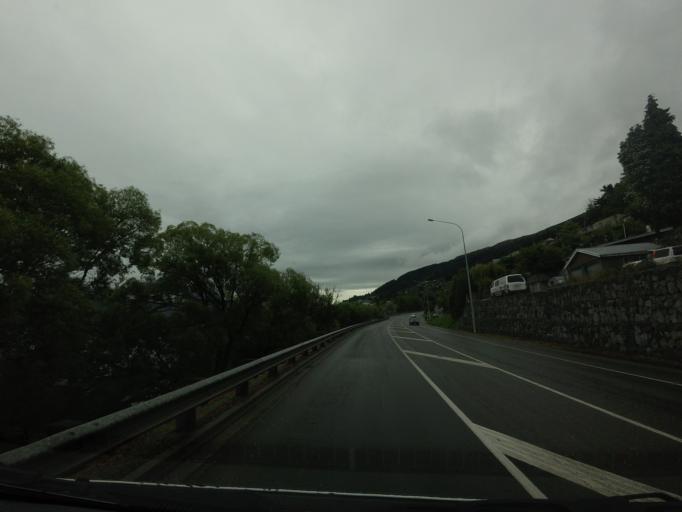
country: NZ
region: Otago
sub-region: Queenstown-Lakes District
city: Queenstown
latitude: -45.0202
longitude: 168.7103
